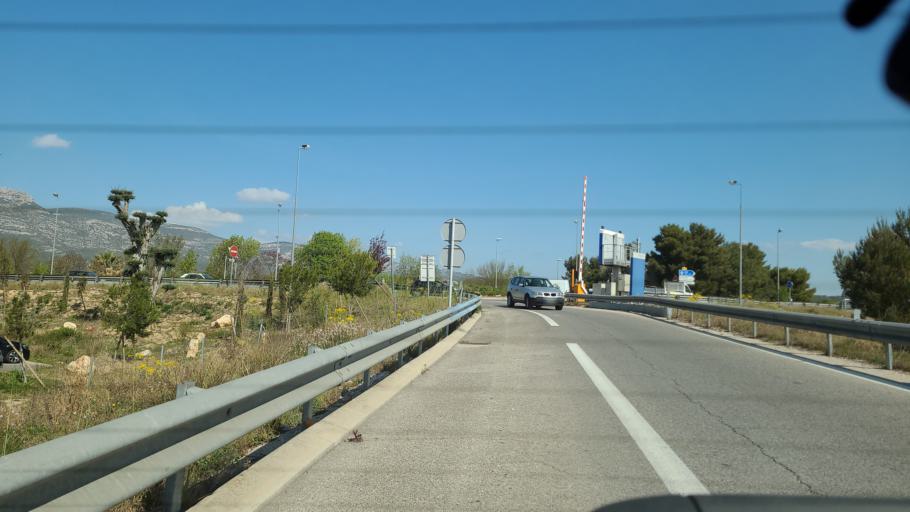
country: FR
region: Provence-Alpes-Cote d'Azur
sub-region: Departement des Bouches-du-Rhone
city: Aubagne
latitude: 43.2972
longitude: 5.5888
